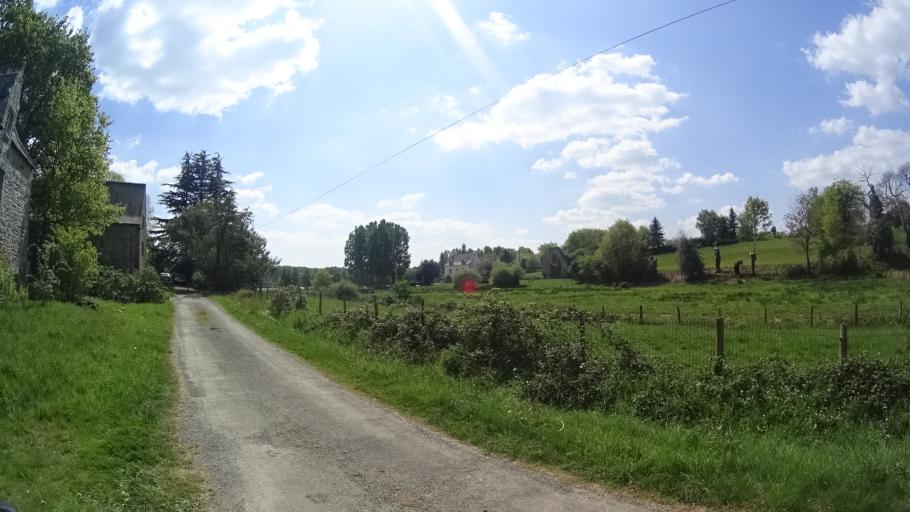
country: FR
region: Brittany
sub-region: Departement du Morbihan
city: Beganne
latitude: 47.5806
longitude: -2.2686
